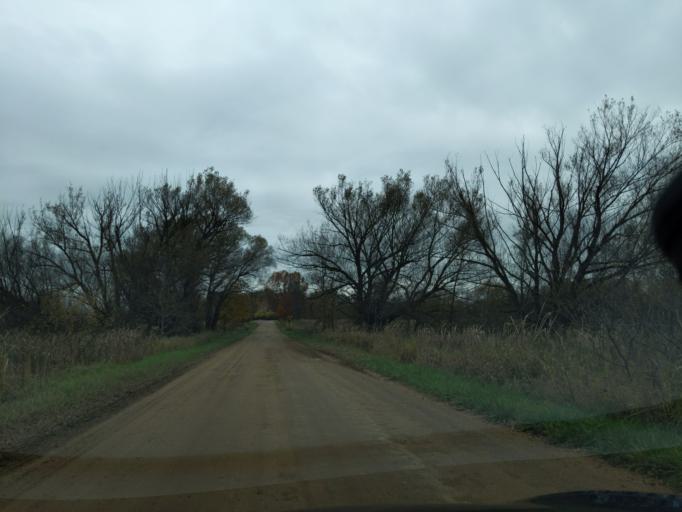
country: US
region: Michigan
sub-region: Eaton County
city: Eaton Rapids
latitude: 42.4174
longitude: -84.6103
